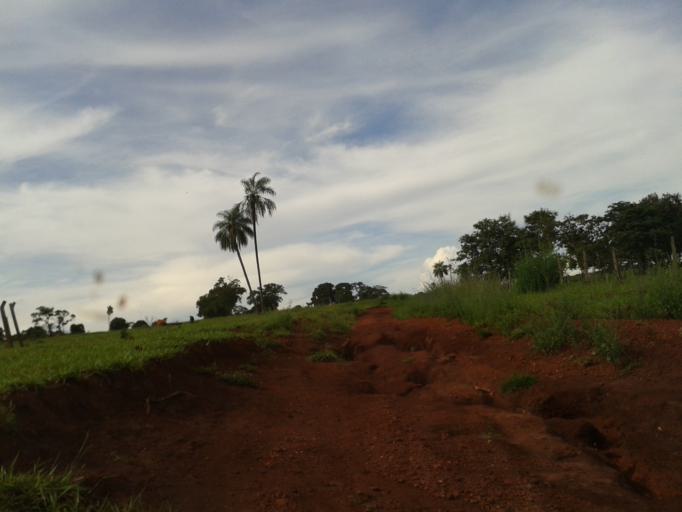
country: BR
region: Minas Gerais
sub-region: Santa Vitoria
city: Santa Vitoria
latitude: -18.7927
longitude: -49.8391
